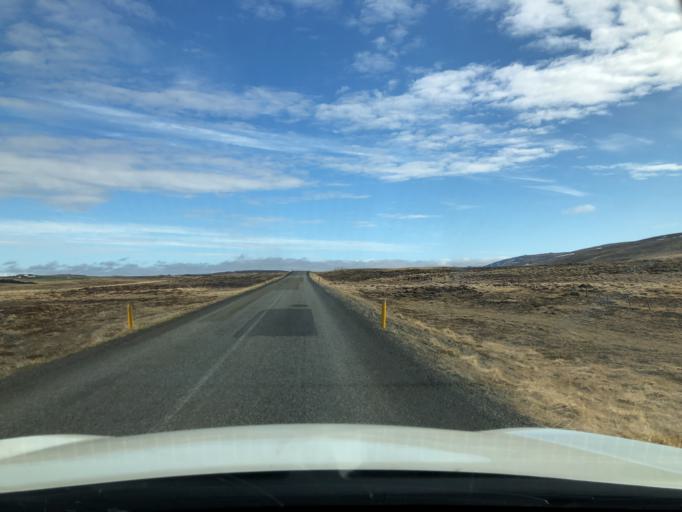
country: IS
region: West
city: Borgarnes
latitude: 65.1020
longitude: -21.7119
